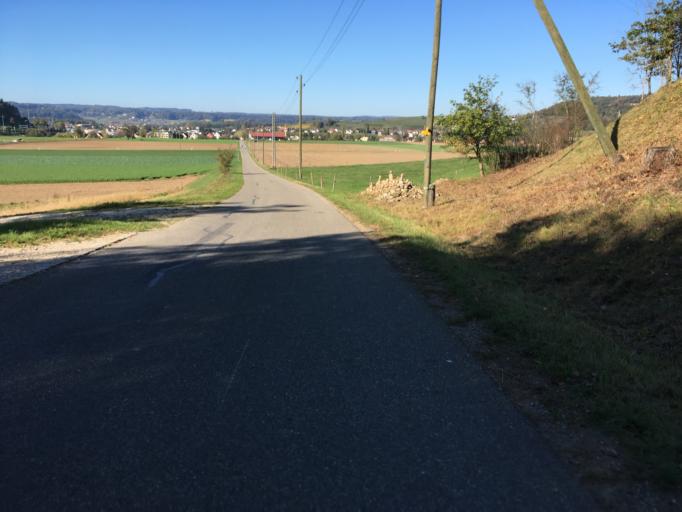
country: CH
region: Zurich
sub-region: Bezirk Buelach
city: Seglingen
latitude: 47.5617
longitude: 8.5277
